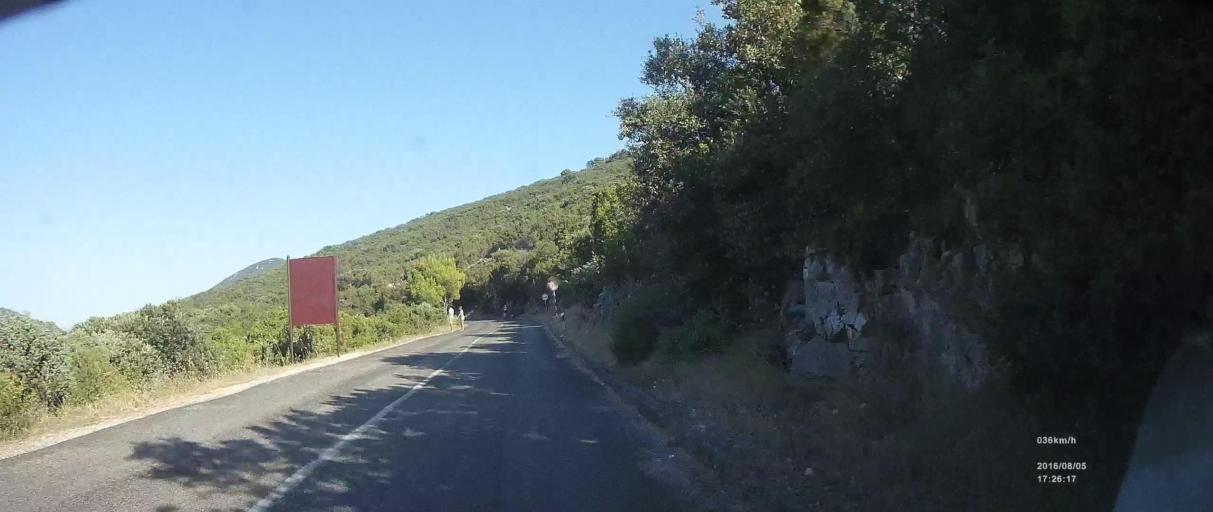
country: HR
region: Dubrovacko-Neretvanska
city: Blato
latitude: 42.7873
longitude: 17.3868
